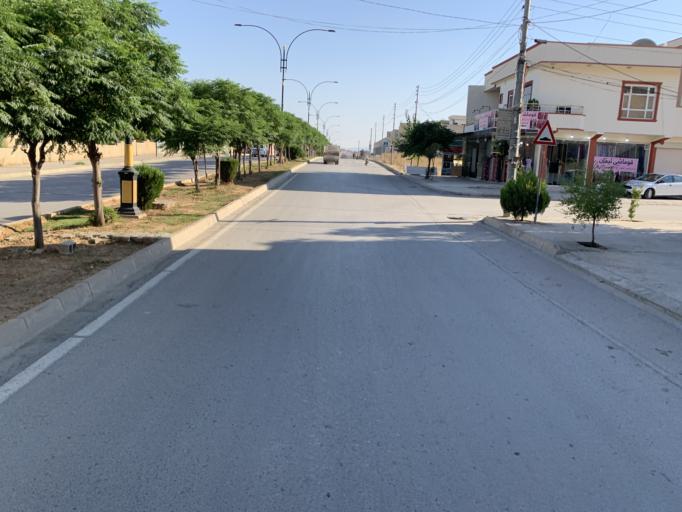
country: IQ
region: As Sulaymaniyah
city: Raniye
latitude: 36.2468
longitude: 44.8749
